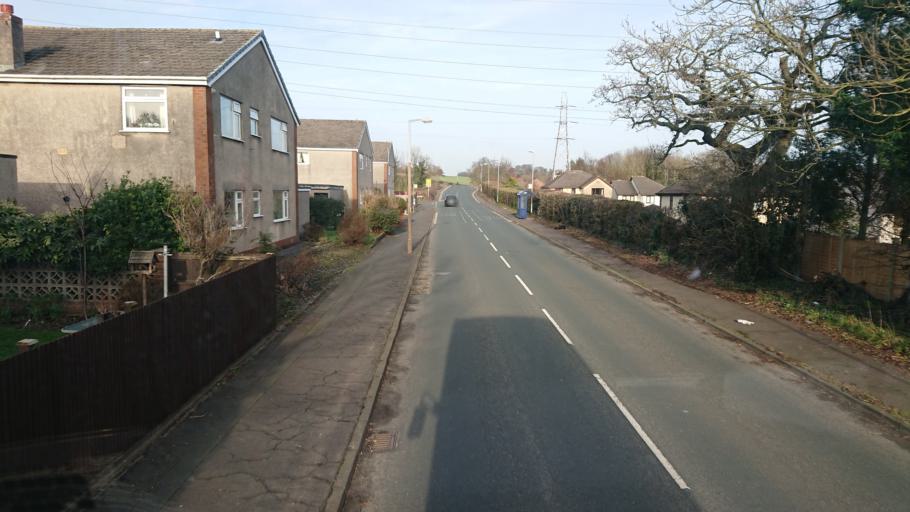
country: GB
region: England
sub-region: Lancashire
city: Bolton le Sands
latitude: 54.0682
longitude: -2.7930
